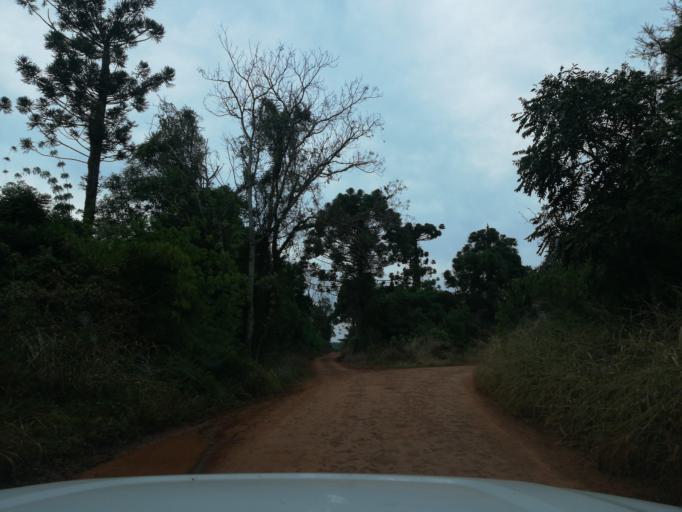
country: AR
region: Misiones
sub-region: Departamento de San Pedro
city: San Pedro
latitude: -26.6320
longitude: -54.0990
